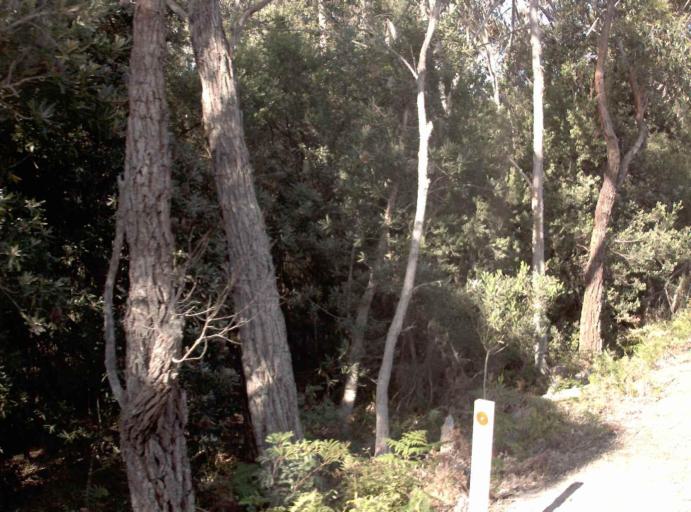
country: AU
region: Victoria
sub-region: East Gippsland
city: Lakes Entrance
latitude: -37.7982
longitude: 148.6850
